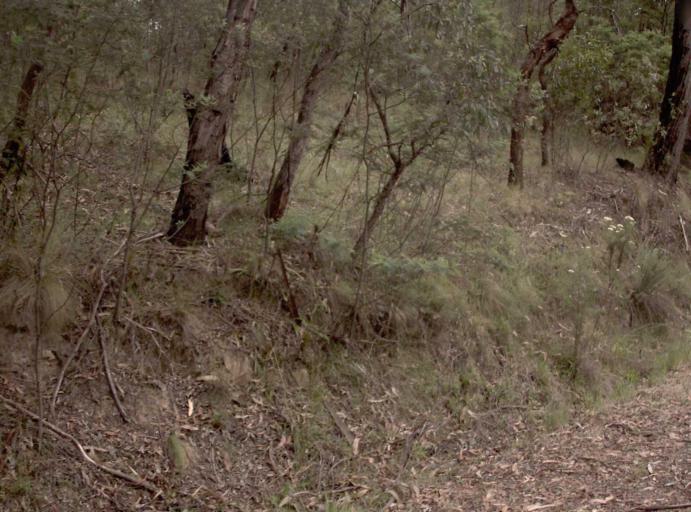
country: AU
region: Victoria
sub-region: East Gippsland
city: Bairnsdale
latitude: -37.6151
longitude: 147.1893
